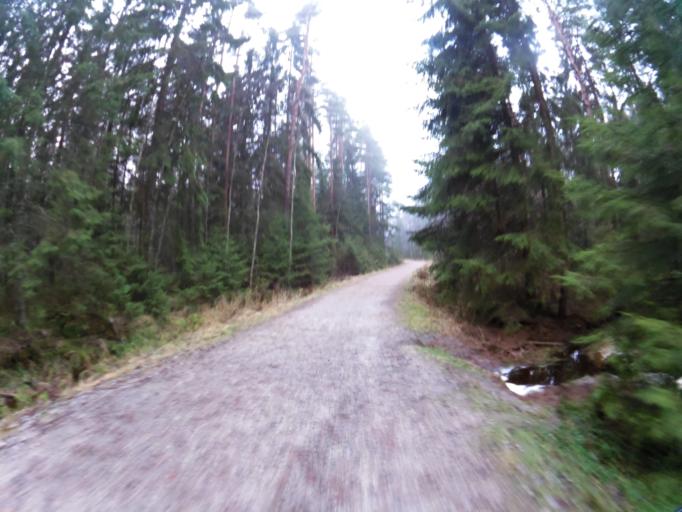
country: NO
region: Ostfold
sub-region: Fredrikstad
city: Fredrikstad
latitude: 59.2663
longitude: 10.9846
